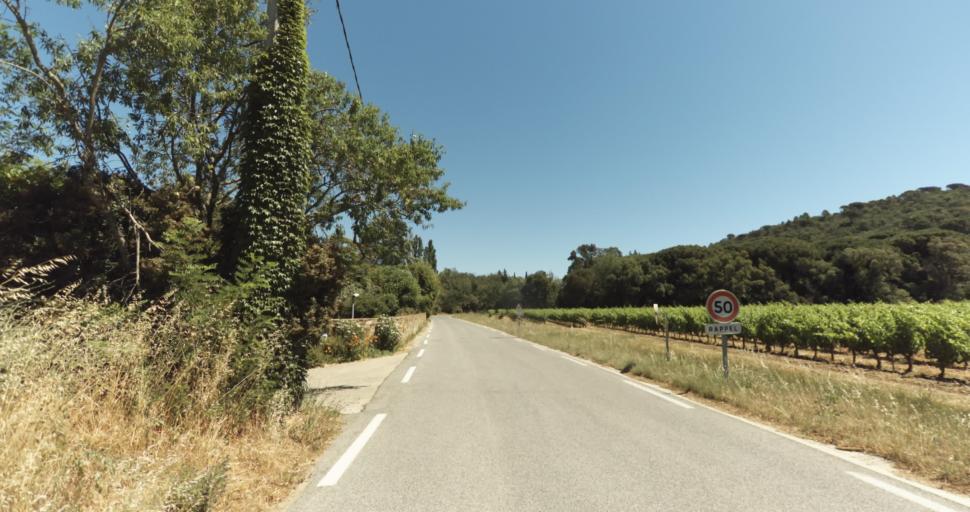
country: FR
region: Provence-Alpes-Cote d'Azur
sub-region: Departement du Var
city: Gassin
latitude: 43.2461
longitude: 6.5774
